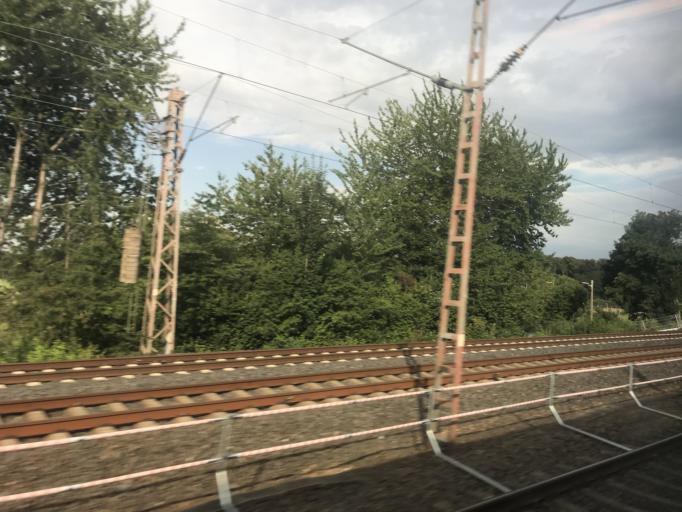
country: DE
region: North Rhine-Westphalia
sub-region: Regierungsbezirk Dusseldorf
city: Dusseldorf
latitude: 51.1945
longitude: 6.8420
